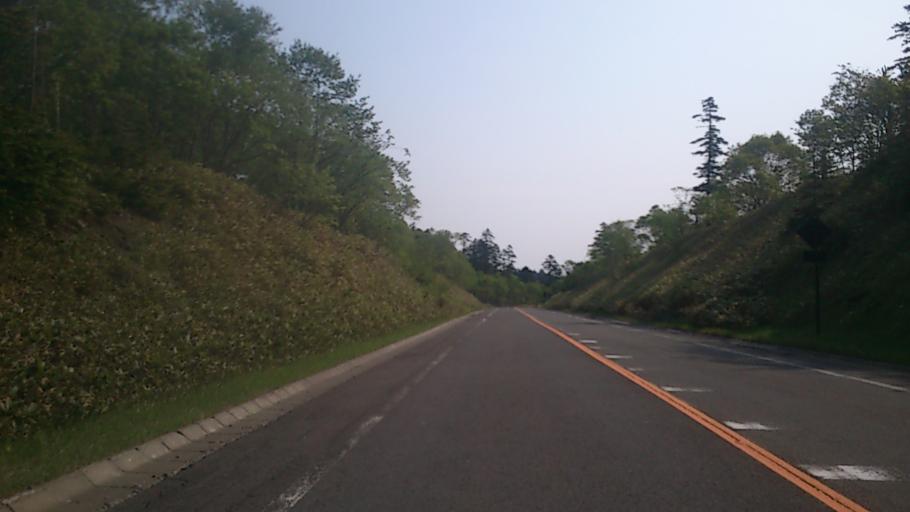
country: JP
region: Hokkaido
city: Bihoro
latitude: 43.4609
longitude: 144.2293
